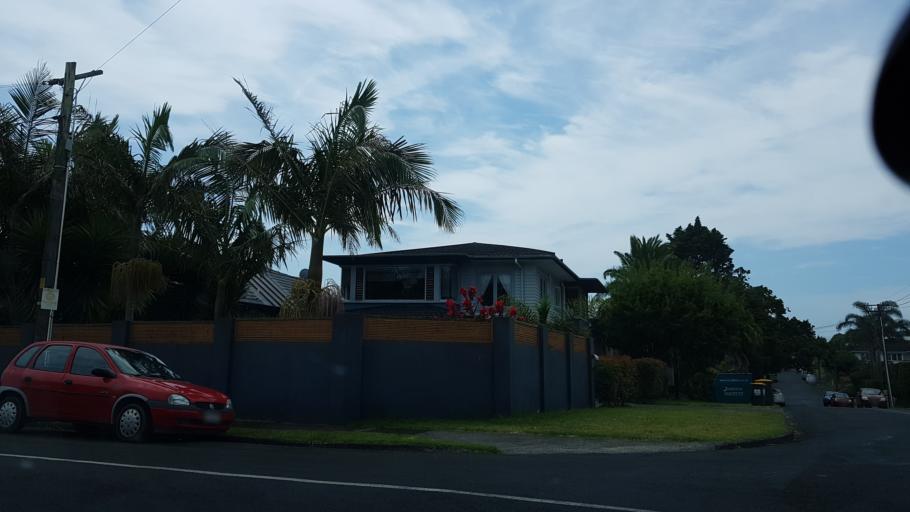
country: NZ
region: Auckland
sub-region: Auckland
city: North Shore
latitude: -36.8011
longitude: 174.7703
